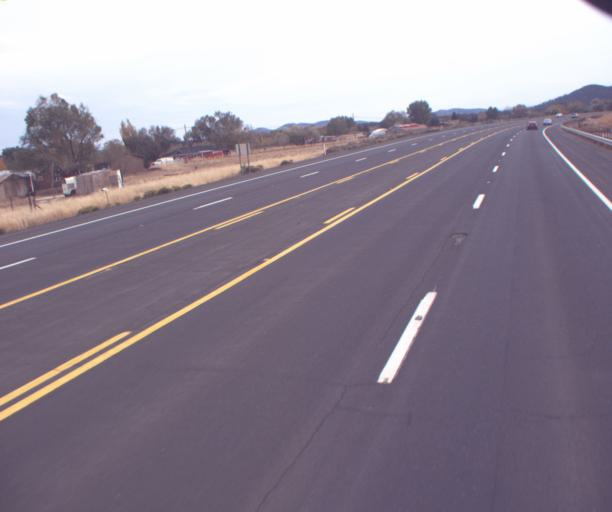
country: US
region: Arizona
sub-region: Coconino County
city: Flagstaff
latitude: 35.3257
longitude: -111.5439
